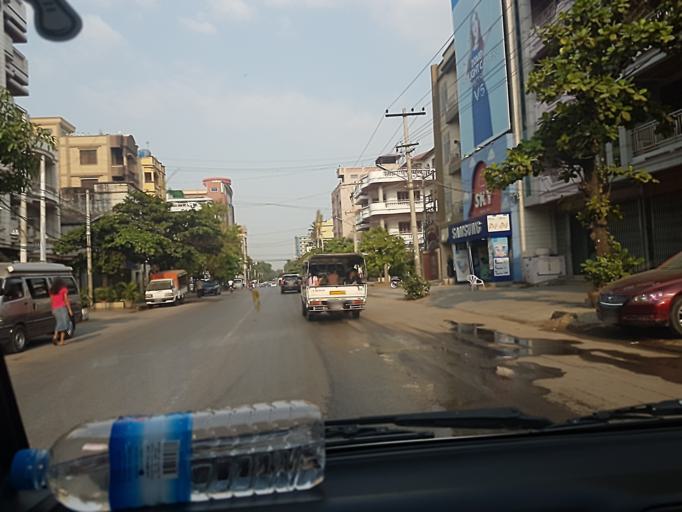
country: MM
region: Mandalay
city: Mandalay
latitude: 21.9887
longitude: 96.0826
